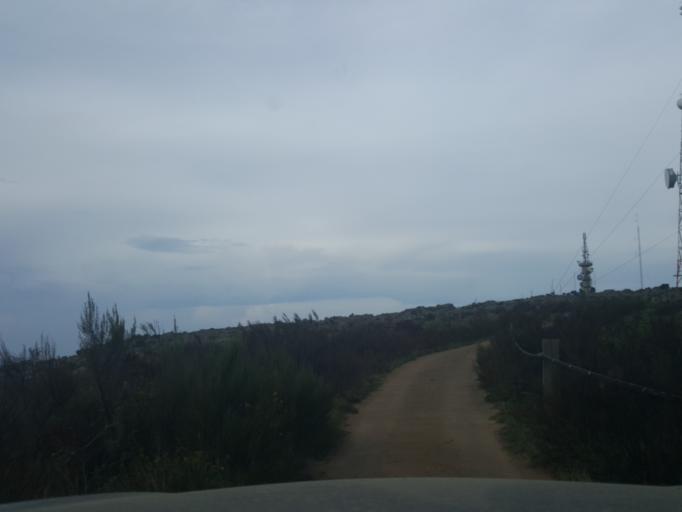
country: ZA
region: Limpopo
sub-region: Mopani District Municipality
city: Hoedspruit
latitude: -24.5425
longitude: 30.8670
